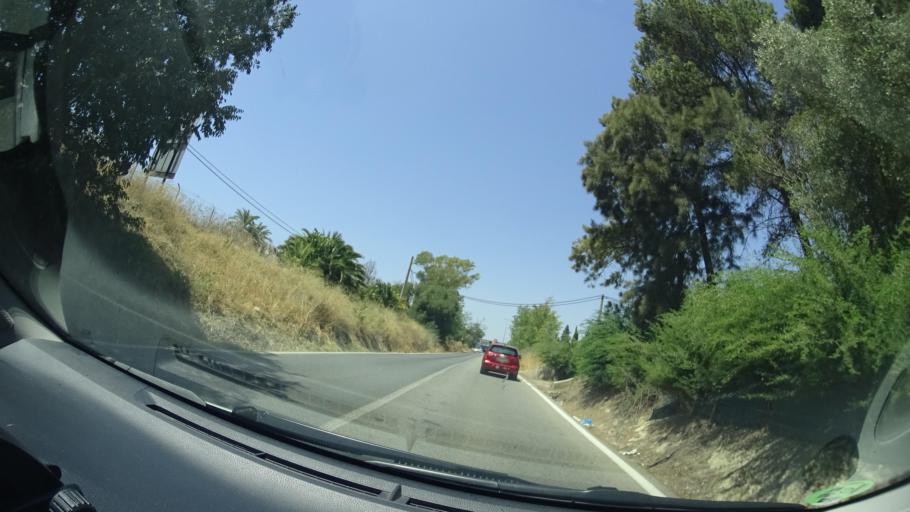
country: ES
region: Andalusia
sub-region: Provincia de Cadiz
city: Jerez de la Frontera
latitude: 36.6696
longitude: -6.1199
